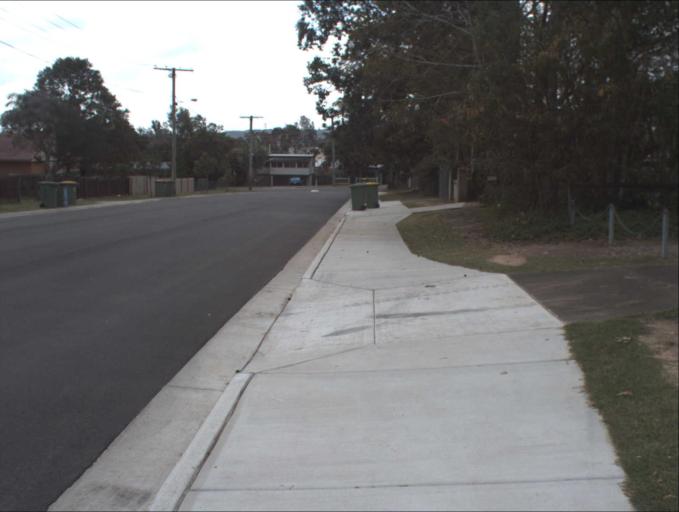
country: AU
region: Queensland
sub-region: Logan
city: Waterford West
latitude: -27.6732
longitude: 153.1423
